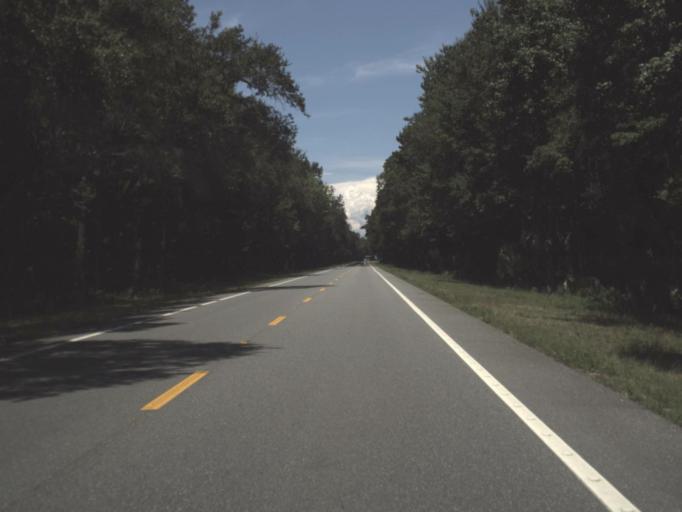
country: US
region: Florida
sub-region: Leon County
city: Woodville
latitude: 30.1439
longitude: -83.9572
